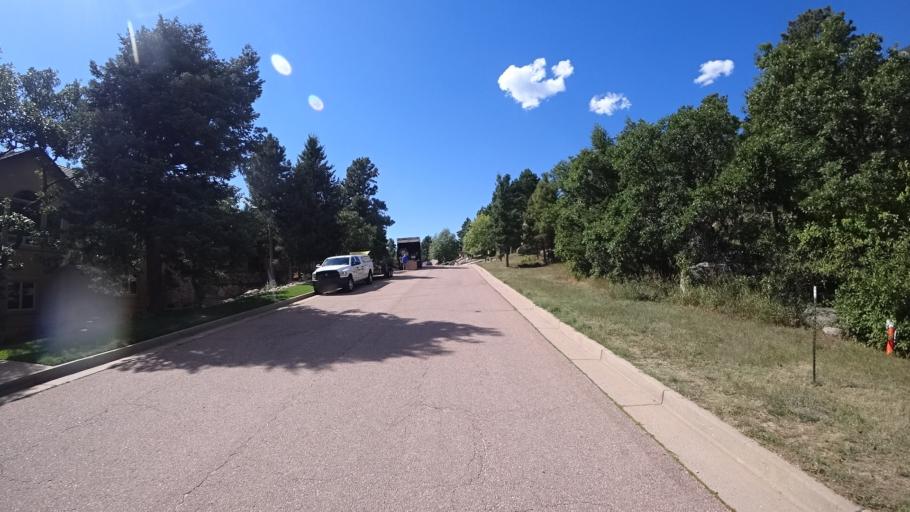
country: US
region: Colorado
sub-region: El Paso County
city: Fort Carson
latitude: 38.7434
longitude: -104.8365
